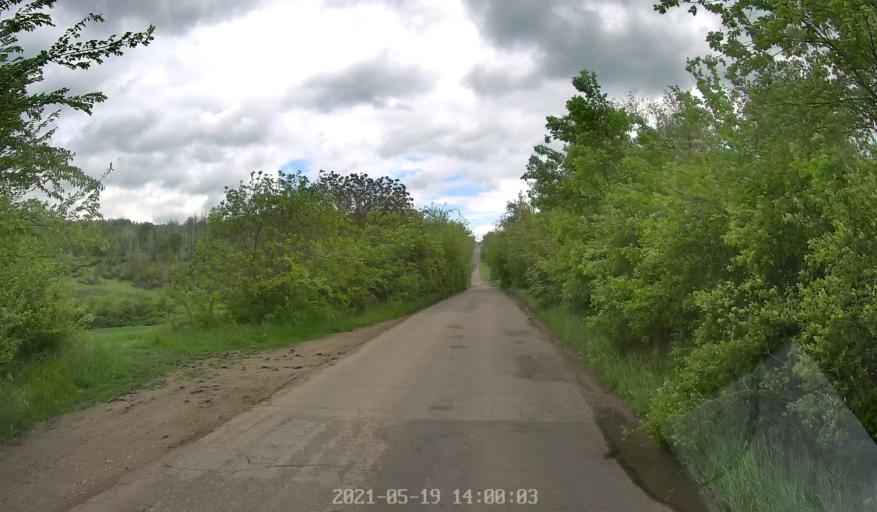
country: MD
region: Chisinau
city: Chisinau
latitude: 47.0370
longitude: 28.9289
